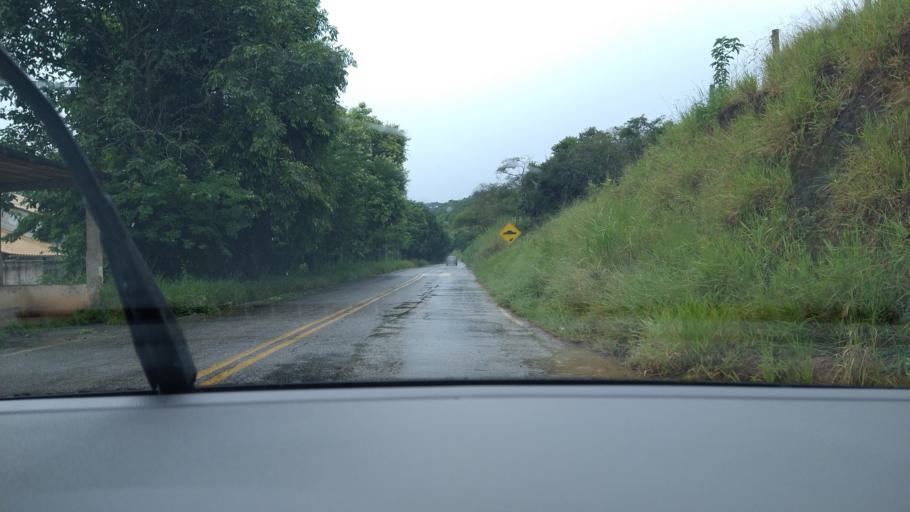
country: BR
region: Minas Gerais
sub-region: Ponte Nova
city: Ponte Nova
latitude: -20.3776
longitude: -42.9001
